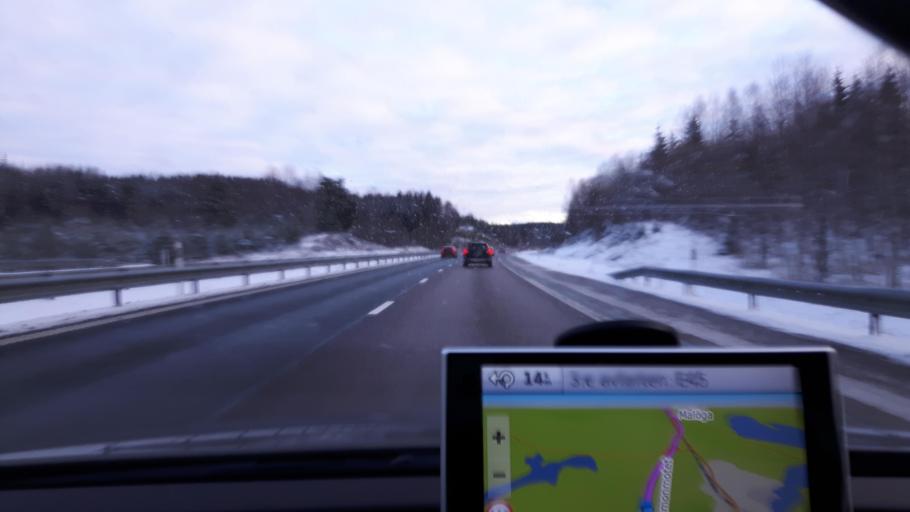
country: SE
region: Vaermland
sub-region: Grums Kommun
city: Slottsbron
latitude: 59.2755
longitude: 13.0157
